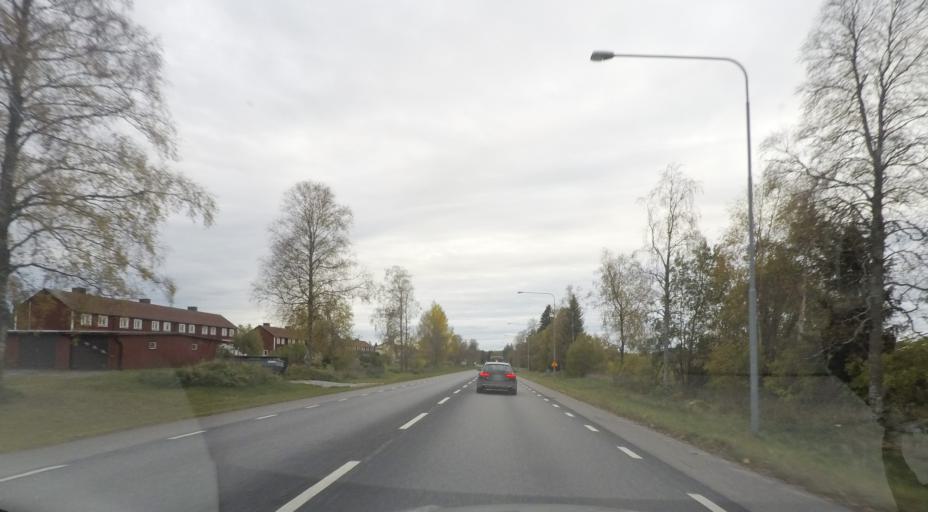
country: SE
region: OErebro
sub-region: Hallefors Kommun
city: Haellefors
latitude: 59.7803
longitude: 14.5296
